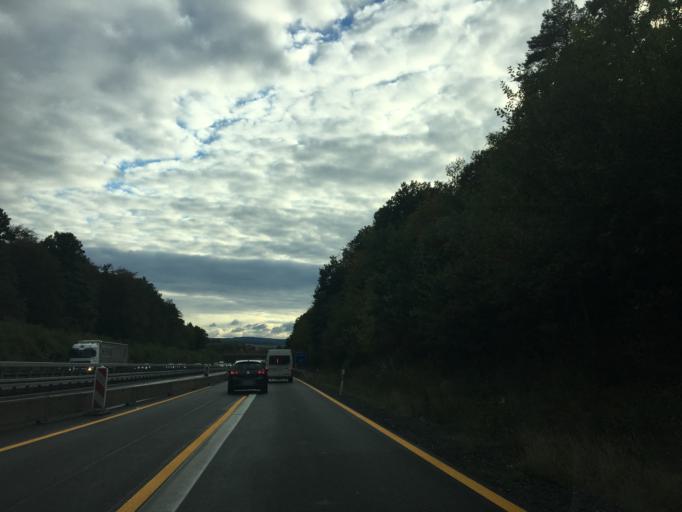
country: DE
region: Hesse
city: Allendorf an der Lahn
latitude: 50.5470
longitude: 8.6539
